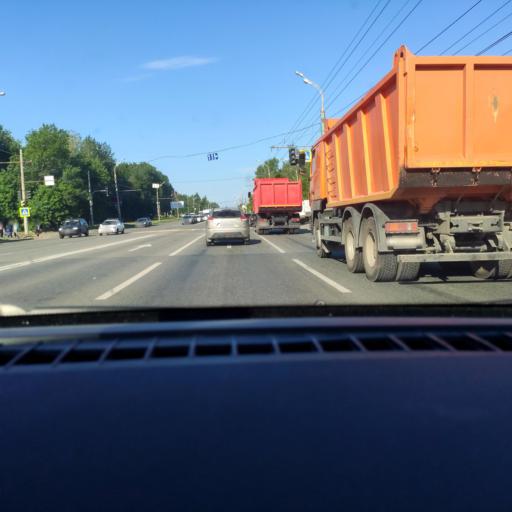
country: RU
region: Udmurtiya
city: Khokhryaki
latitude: 56.8915
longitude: 53.2626
